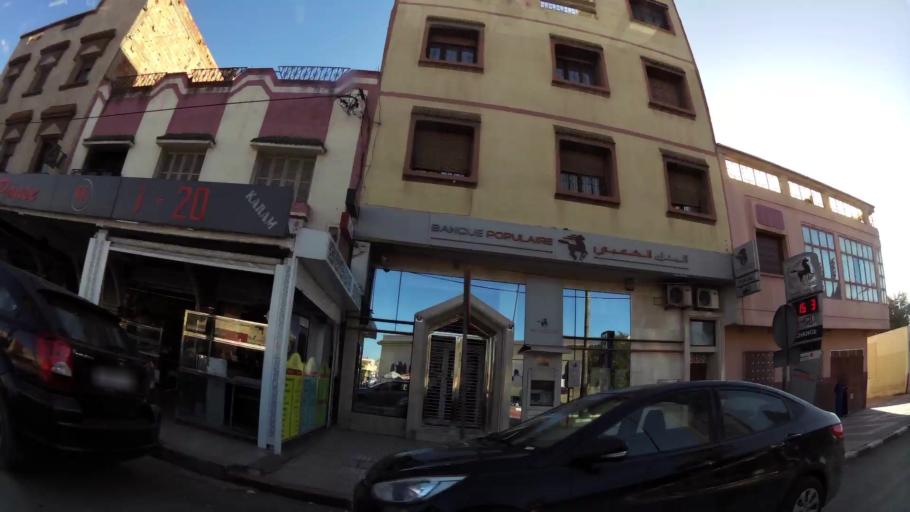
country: MA
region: Meknes-Tafilalet
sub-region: Meknes
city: Meknes
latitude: 33.8787
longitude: -5.5618
